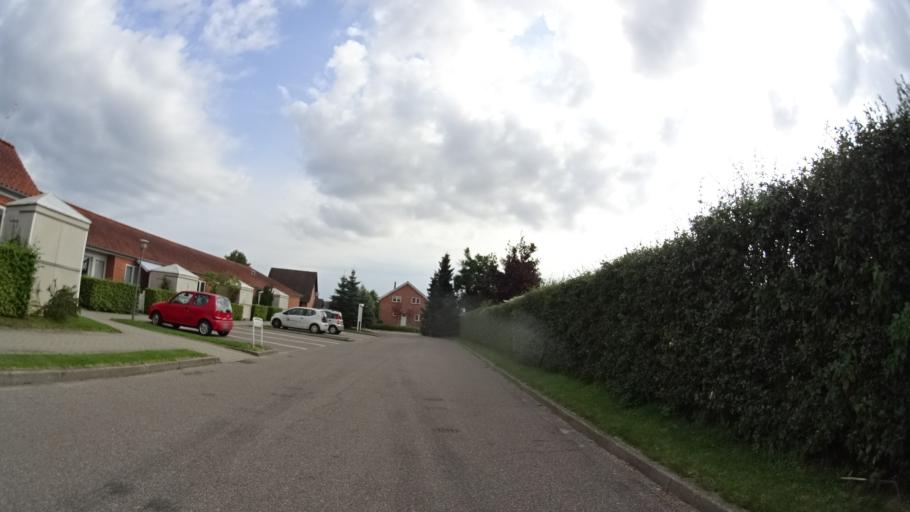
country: DK
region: Central Jutland
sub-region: Arhus Kommune
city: Stavtrup
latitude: 56.1523
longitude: 10.0945
